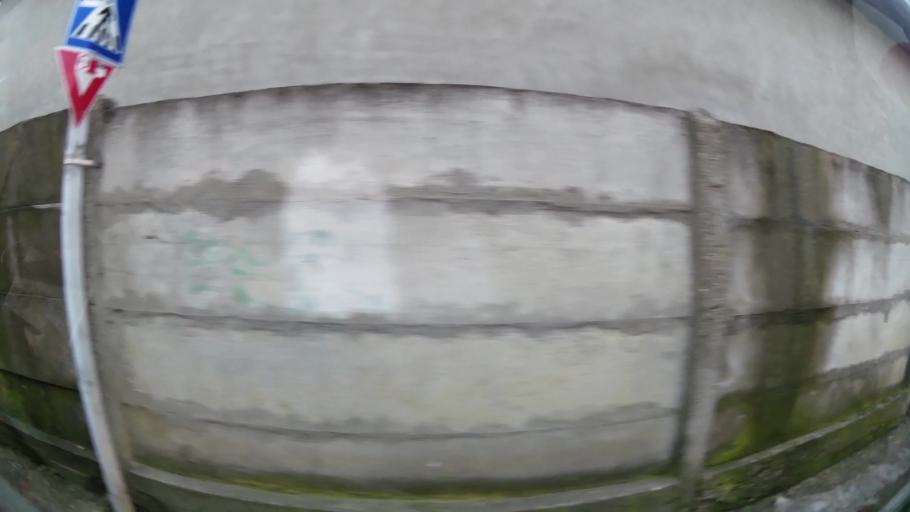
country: RO
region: Ilfov
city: Dobroesti
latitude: 44.4547
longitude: 26.1794
